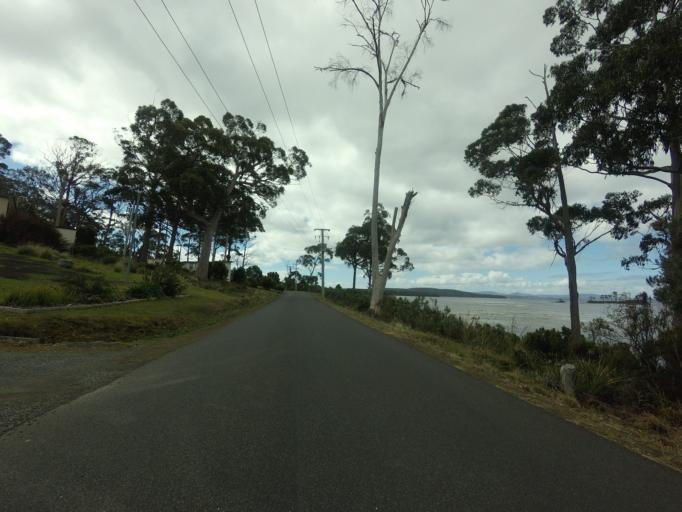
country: AU
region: Tasmania
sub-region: Huon Valley
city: Geeveston
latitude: -43.4459
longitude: 146.9606
